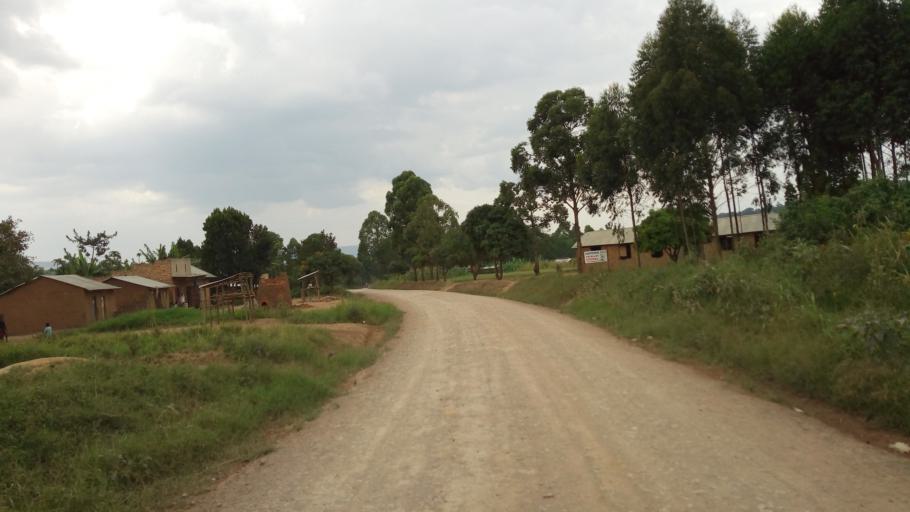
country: UG
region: Central Region
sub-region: Kiboga District
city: Kiboga
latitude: 0.7109
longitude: 31.7594
